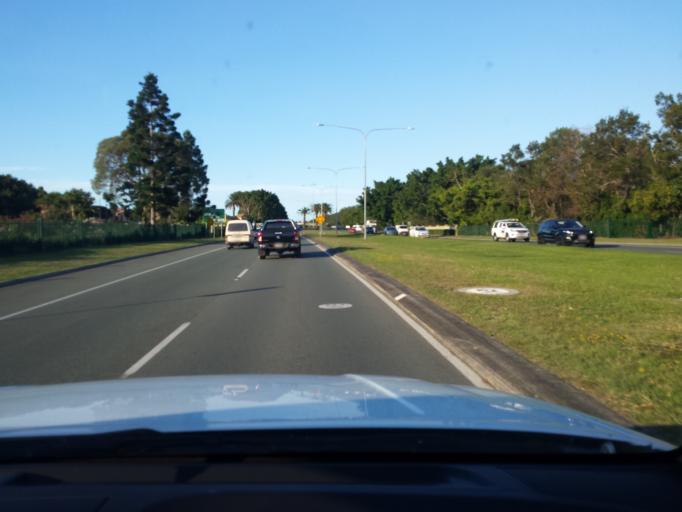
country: AU
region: Queensland
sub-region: Gold Coast
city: Oxenford
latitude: -27.8797
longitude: 153.3365
